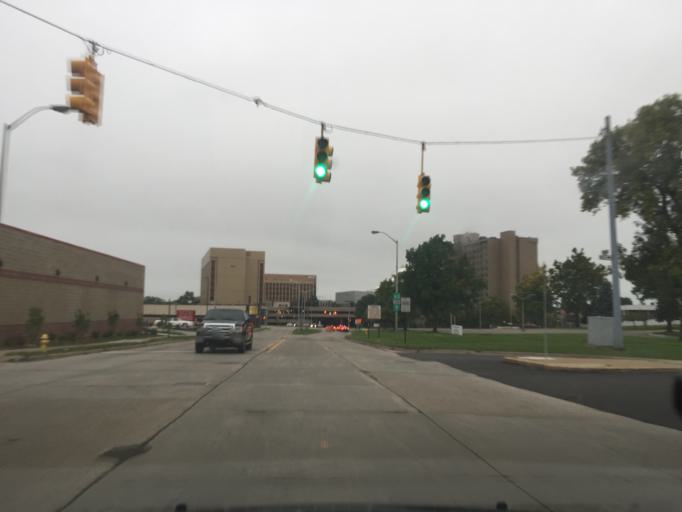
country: US
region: Michigan
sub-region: Oakland County
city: Pontiac
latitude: 42.6343
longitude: -83.2858
